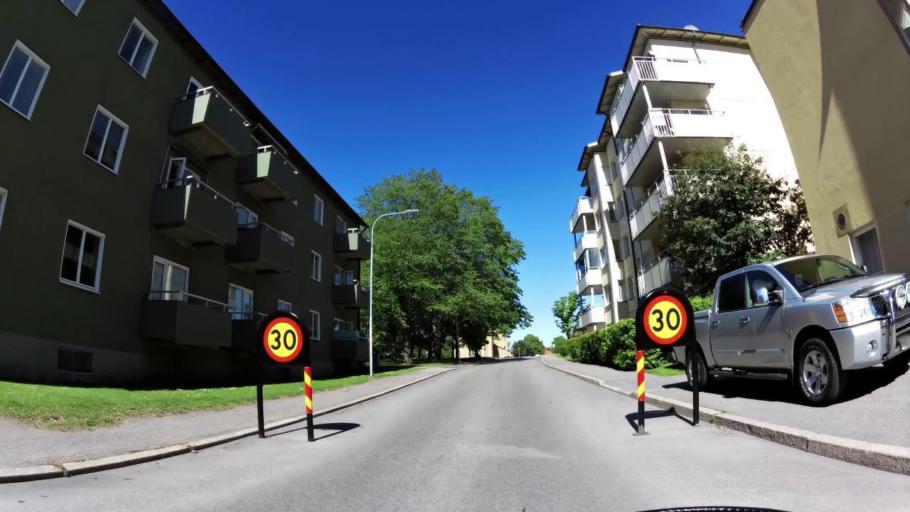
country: SE
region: OEstergoetland
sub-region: Linkopings Kommun
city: Linkoping
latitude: 58.4080
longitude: 15.6397
